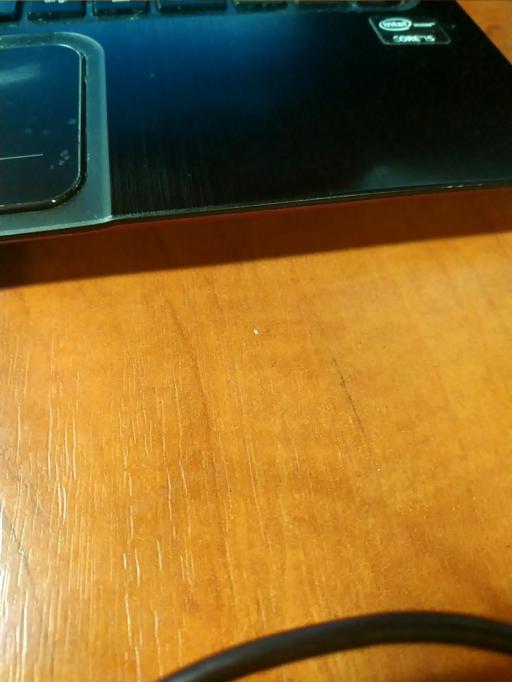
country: RU
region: Tverskaya
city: Likhoslavl'
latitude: 56.9525
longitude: 35.5198
